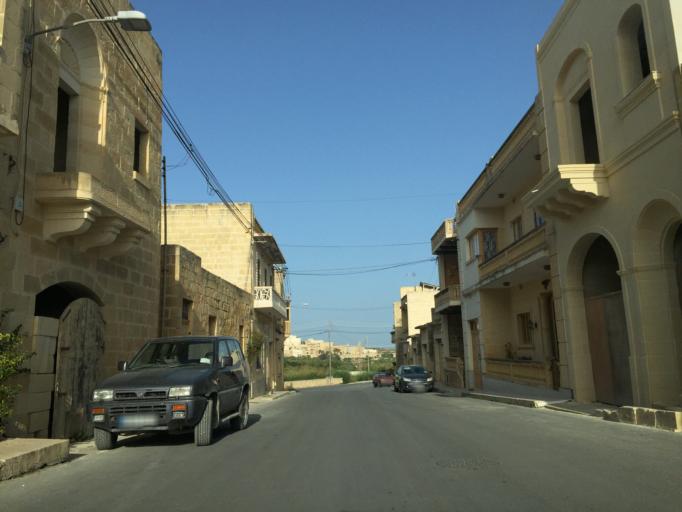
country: MT
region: Il-Qala
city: Qala
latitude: 36.0353
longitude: 14.3135
